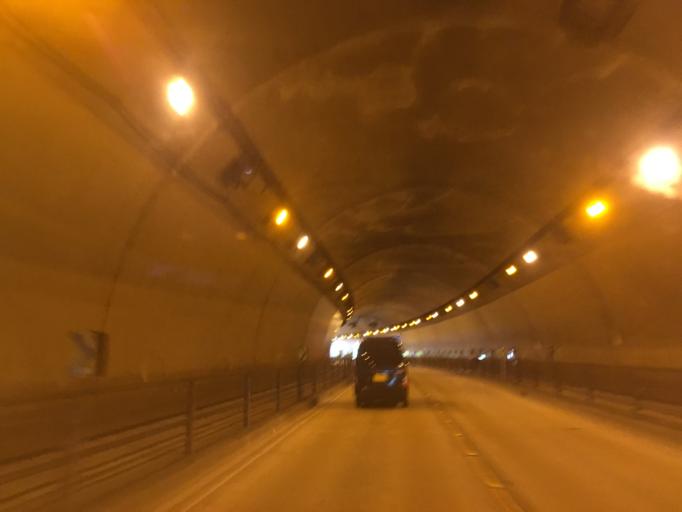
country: JP
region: Tokyo
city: Hino
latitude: 35.6403
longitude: 139.3879
